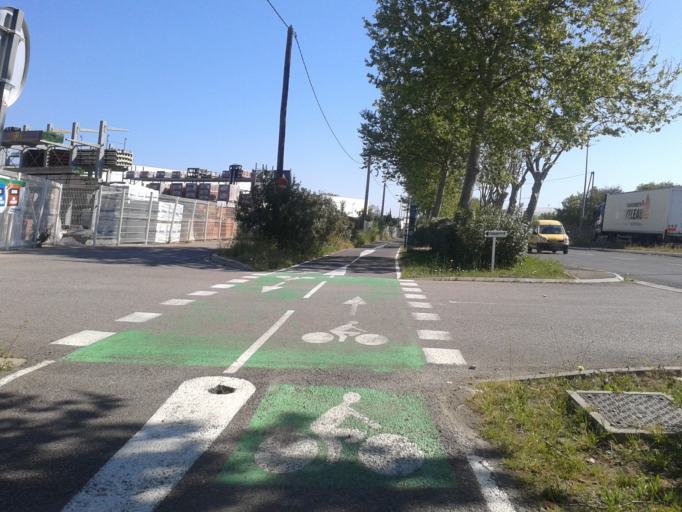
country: FR
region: Languedoc-Roussillon
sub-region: Departement des Pyrenees-Orientales
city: Perpignan
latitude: 42.6867
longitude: 2.8694
